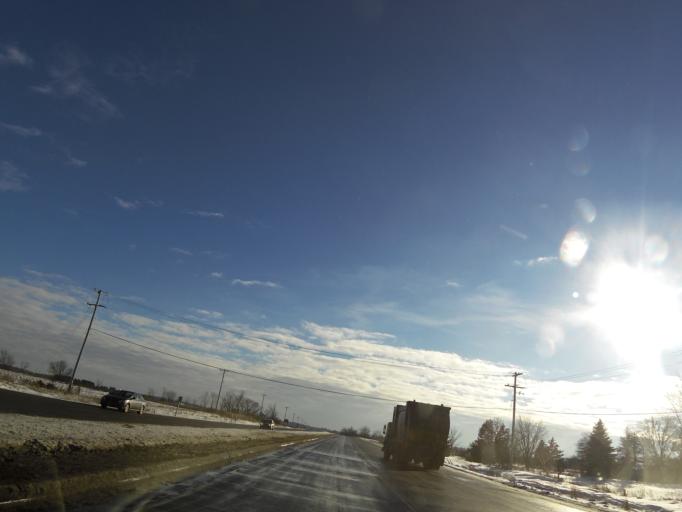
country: US
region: Wisconsin
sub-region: Saint Croix County
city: North Hudson
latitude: 44.9864
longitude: -92.6803
